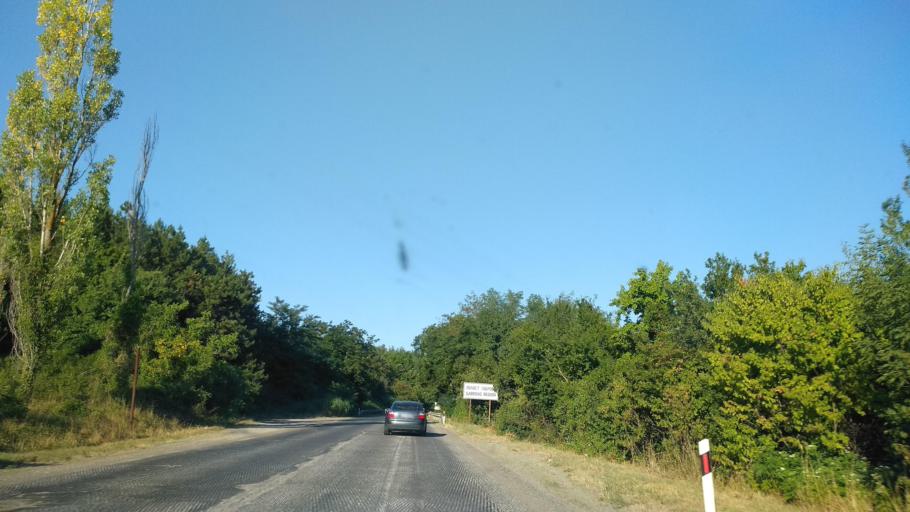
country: BG
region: Veliko Turnovo
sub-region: Obshtina Pavlikeni
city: Byala Cherkva
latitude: 43.0686
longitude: 25.3065
